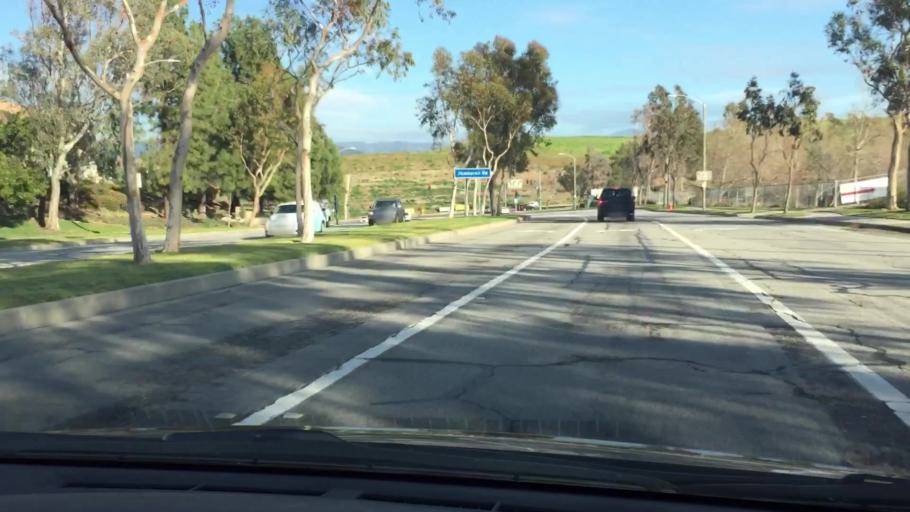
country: US
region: California
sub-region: Orange County
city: North Tustin
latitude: 33.7959
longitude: -117.7632
